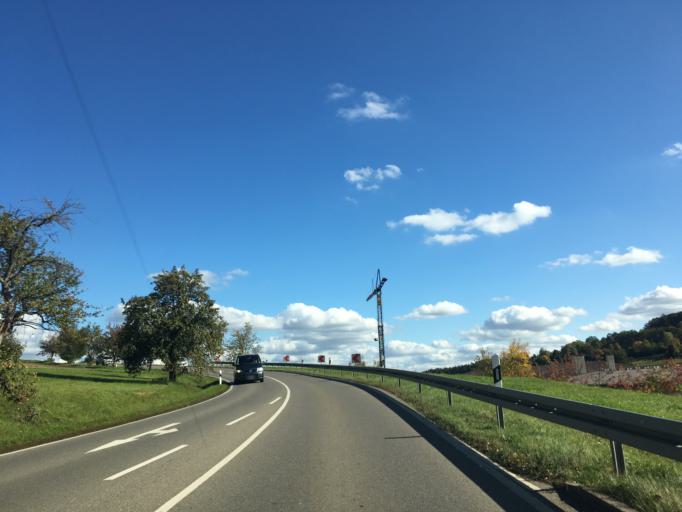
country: DE
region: Baden-Wuerttemberg
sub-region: Karlsruhe Region
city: Ostelsheim
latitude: 48.7270
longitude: 8.8554
